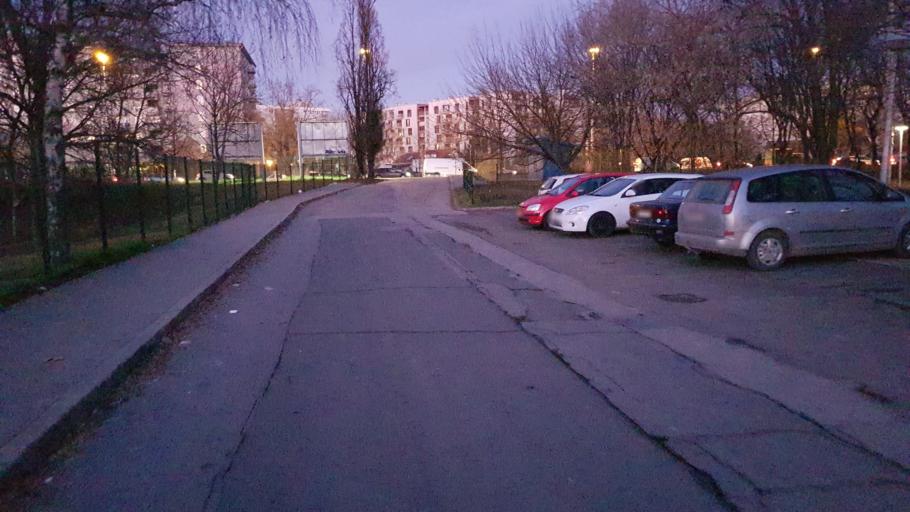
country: HR
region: Grad Zagreb
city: Novi Zagreb
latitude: 45.7864
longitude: 15.9465
